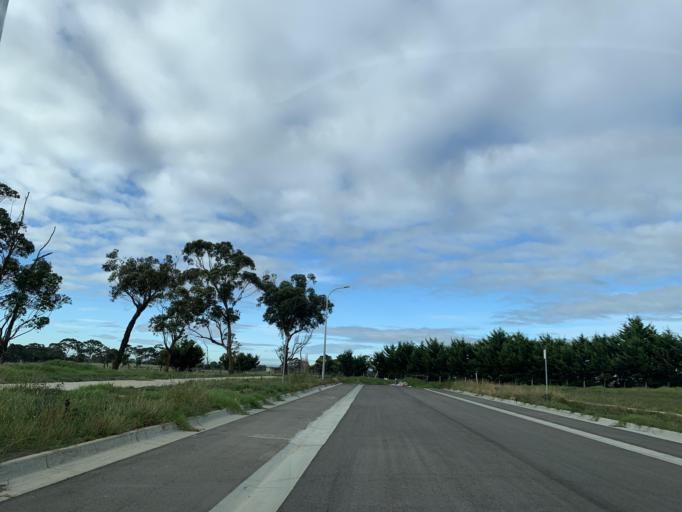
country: AU
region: Victoria
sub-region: Casey
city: Junction Village
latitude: -38.1305
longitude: 145.3366
